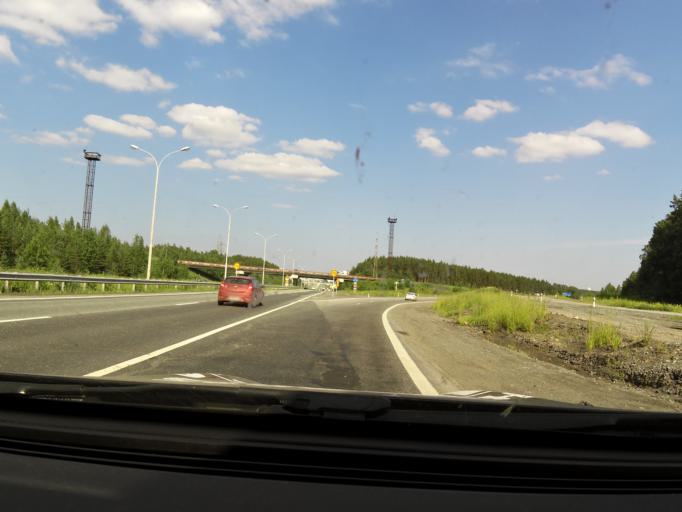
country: RU
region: Sverdlovsk
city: Shirokaya Rechka
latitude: 56.8255
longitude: 60.4873
